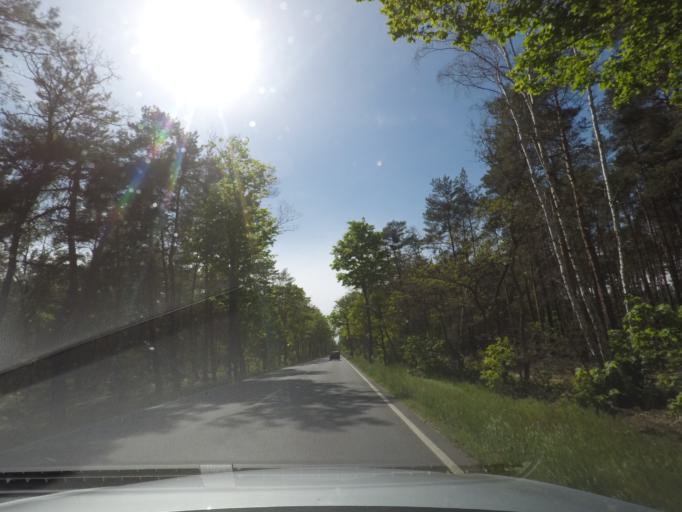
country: DE
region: Brandenburg
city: Luebben
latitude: 51.9462
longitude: 13.8412
